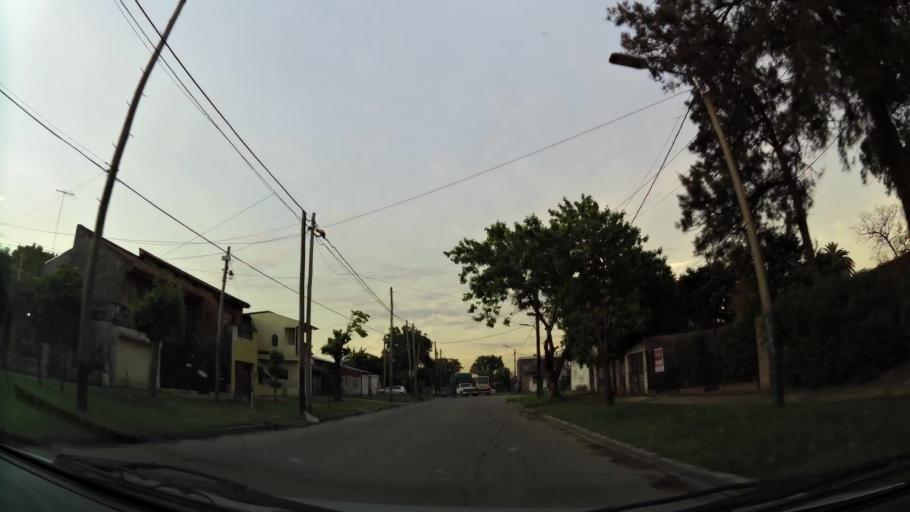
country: AR
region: Buenos Aires
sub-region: Partido de Lomas de Zamora
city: Lomas de Zamora
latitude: -34.7580
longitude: -58.3686
